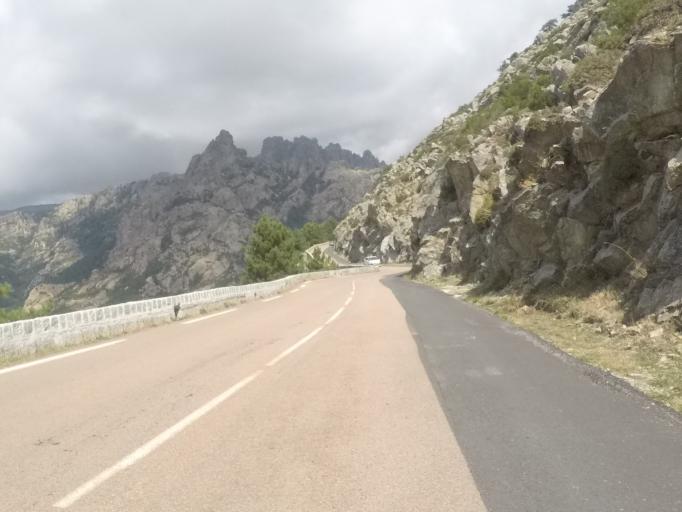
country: FR
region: Corsica
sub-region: Departement de la Corse-du-Sud
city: Zonza
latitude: 41.7825
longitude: 9.2192
